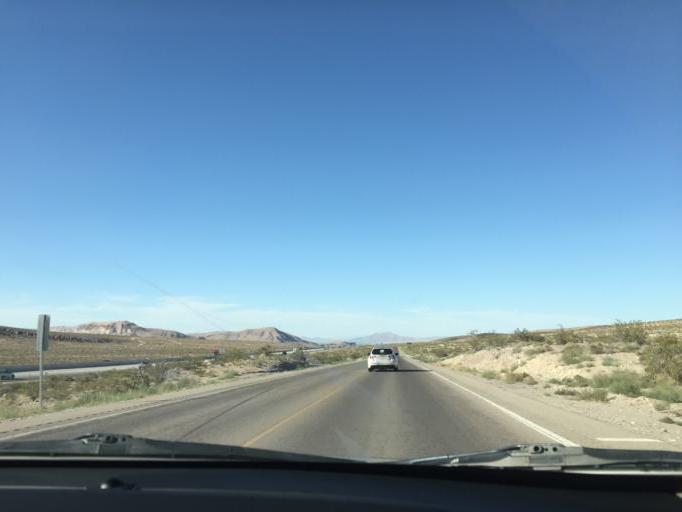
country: US
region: Nevada
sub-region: Clark County
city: Enterprise
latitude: 35.8943
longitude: -115.2177
